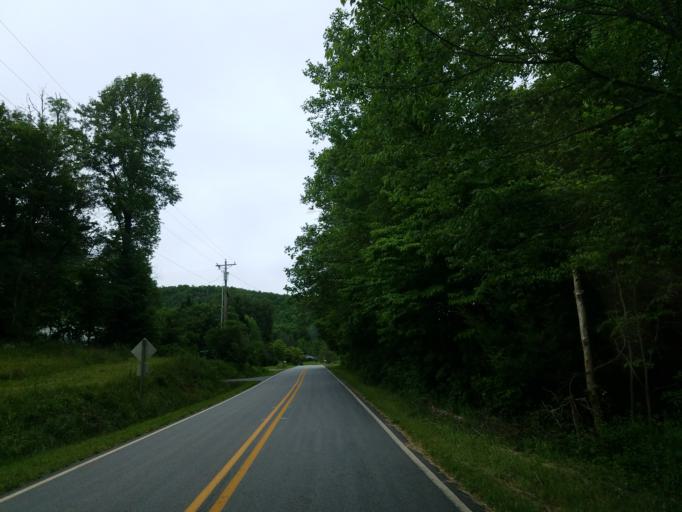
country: US
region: Georgia
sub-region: Union County
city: Blairsville
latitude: 34.7120
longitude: -83.9973
